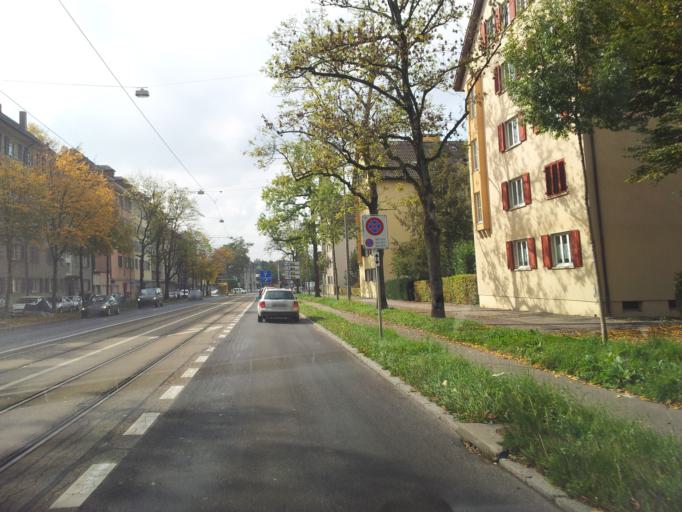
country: CH
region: Bern
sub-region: Bern-Mittelland District
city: Muri
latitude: 46.9428
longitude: 7.4687
